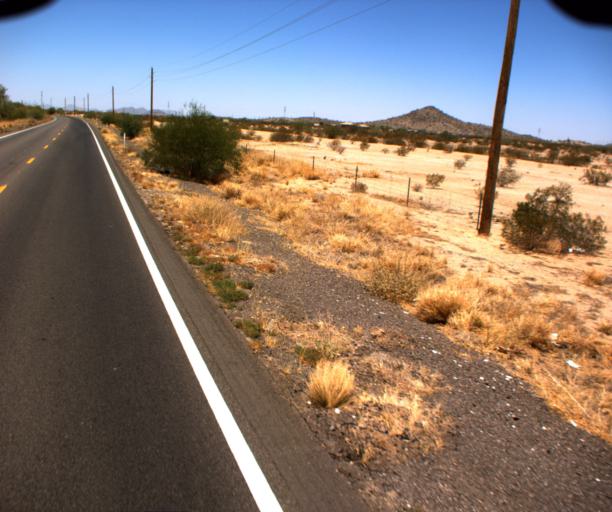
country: US
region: Arizona
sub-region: Pinal County
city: Maricopa
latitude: 33.0736
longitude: -112.1868
